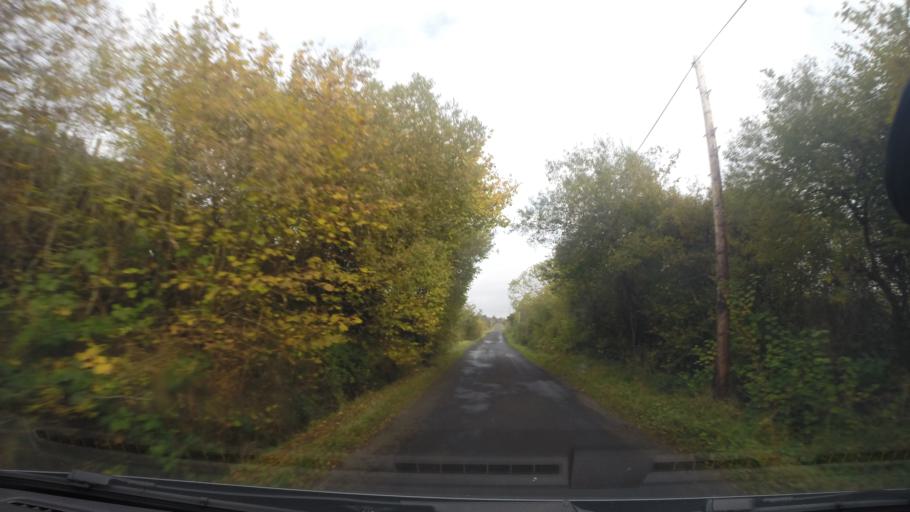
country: IE
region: Ulster
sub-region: County Donegal
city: Ballyshannon
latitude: 54.4207
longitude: -8.0041
